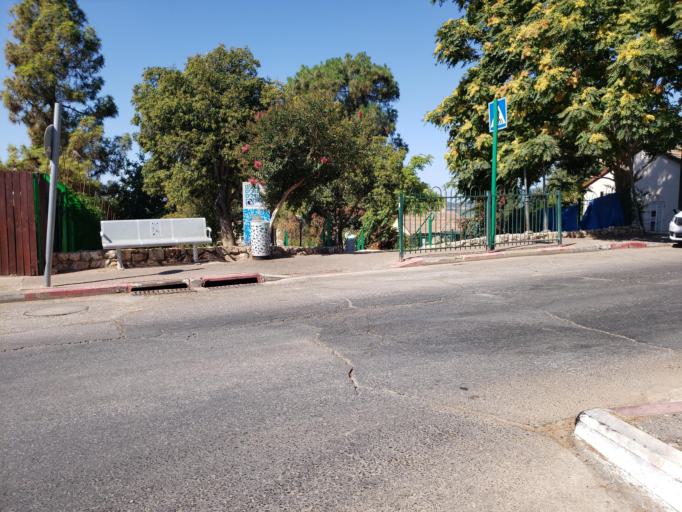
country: IL
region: Northern District
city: Safed
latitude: 32.9602
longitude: 35.4960
